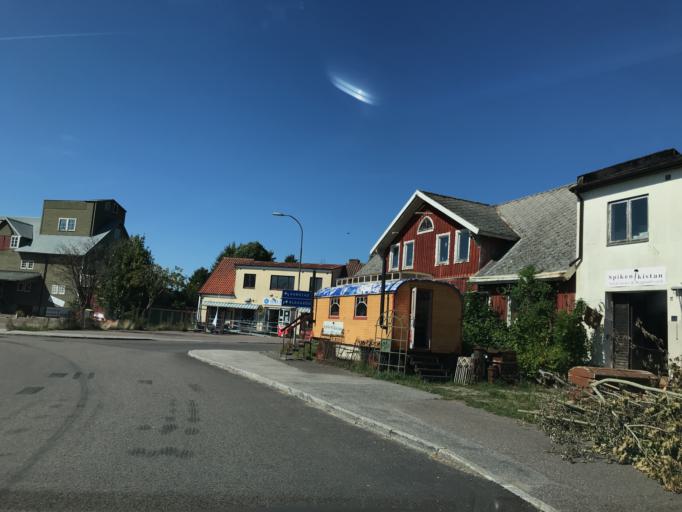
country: SE
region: Skane
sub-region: Tomelilla Kommun
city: Tomelilla
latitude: 55.6553
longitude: 13.8906
